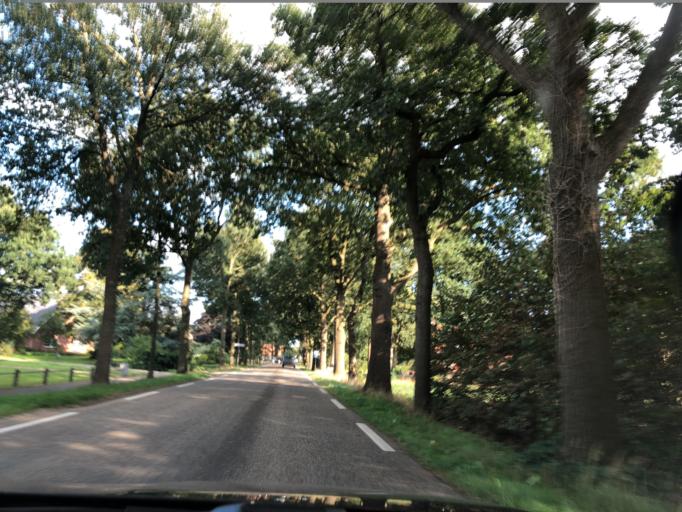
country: NL
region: Groningen
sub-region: Gemeente Vlagtwedde
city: Vlagtwedde
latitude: 53.0223
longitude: 7.1693
